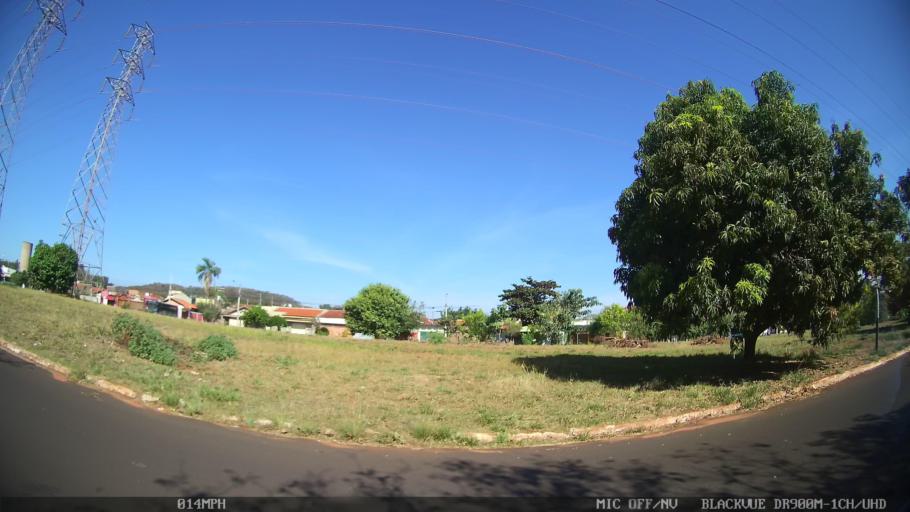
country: BR
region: Sao Paulo
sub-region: Ribeirao Preto
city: Ribeirao Preto
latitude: -21.2230
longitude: -47.7634
